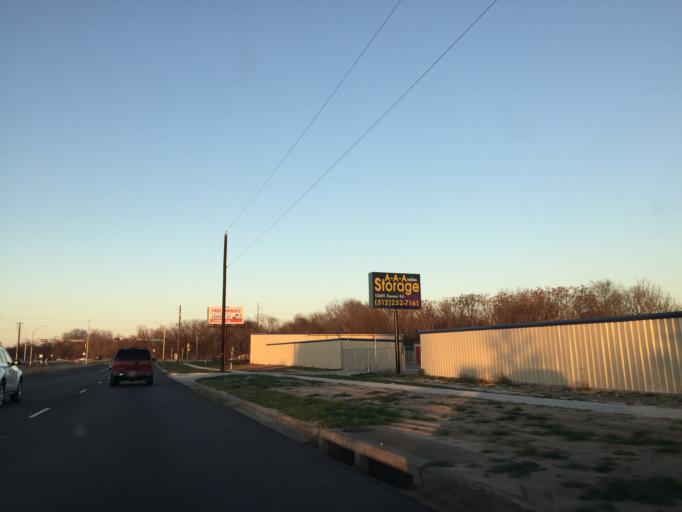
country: US
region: Texas
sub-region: Travis County
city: Pflugerville
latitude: 30.4055
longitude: -97.6370
